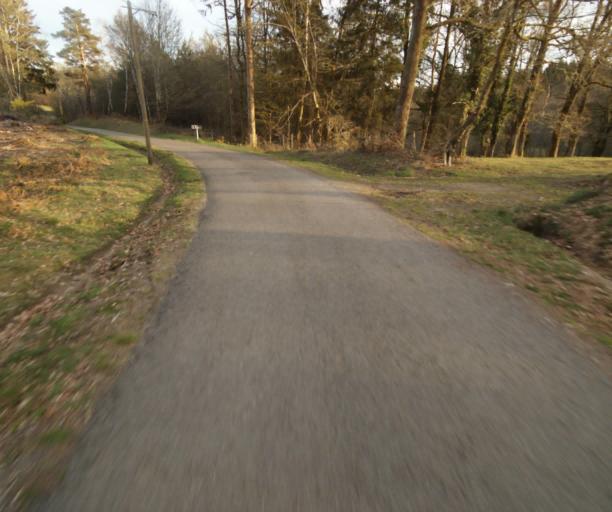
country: FR
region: Limousin
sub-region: Departement de la Correze
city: Argentat
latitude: 45.2253
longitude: 1.9702
